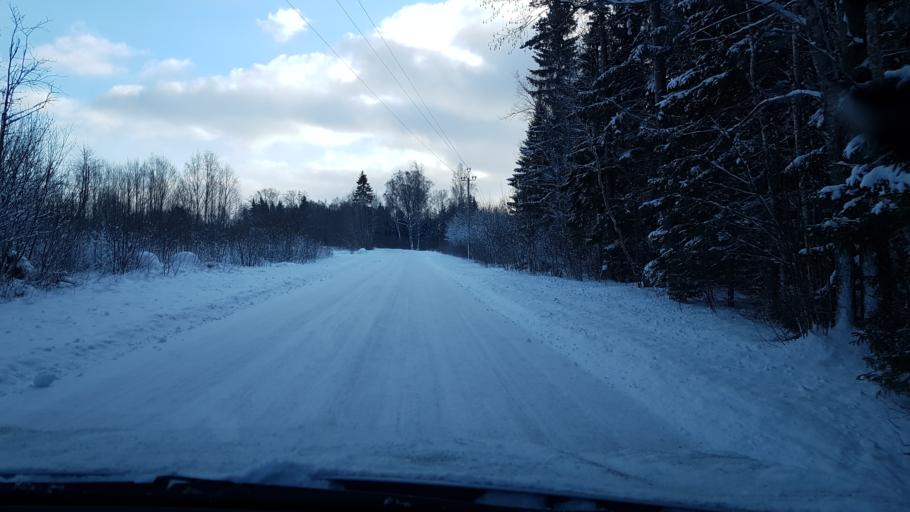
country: EE
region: Harju
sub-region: Nissi vald
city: Turba
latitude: 59.1548
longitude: 24.1445
